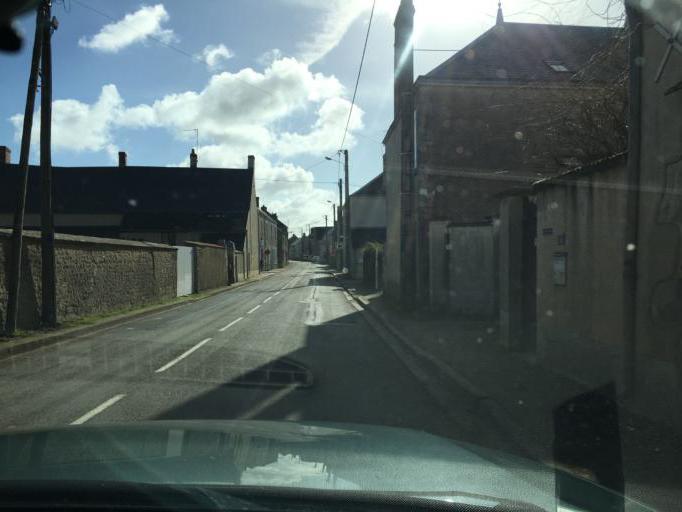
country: FR
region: Centre
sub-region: Departement du Loiret
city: Beaugency
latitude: 47.8299
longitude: 1.5708
